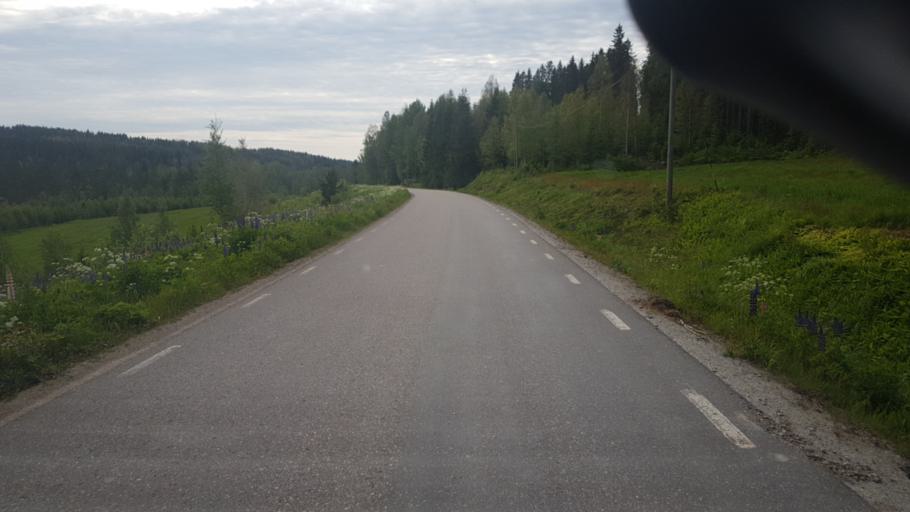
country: SE
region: Vaermland
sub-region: Arvika Kommun
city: Arvika
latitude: 59.7824
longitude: 12.7697
